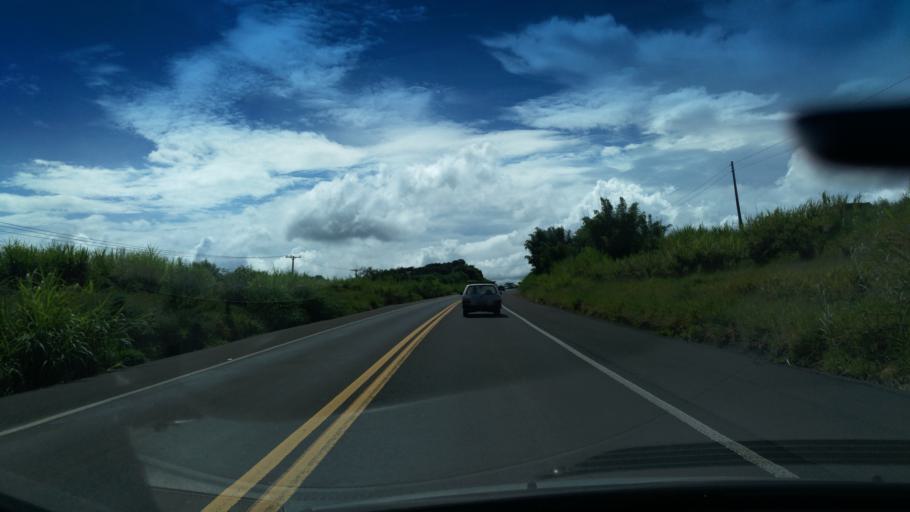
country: BR
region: Sao Paulo
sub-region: Santo Antonio Do Jardim
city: Espirito Santo do Pinhal
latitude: -22.1629
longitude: -46.7341
